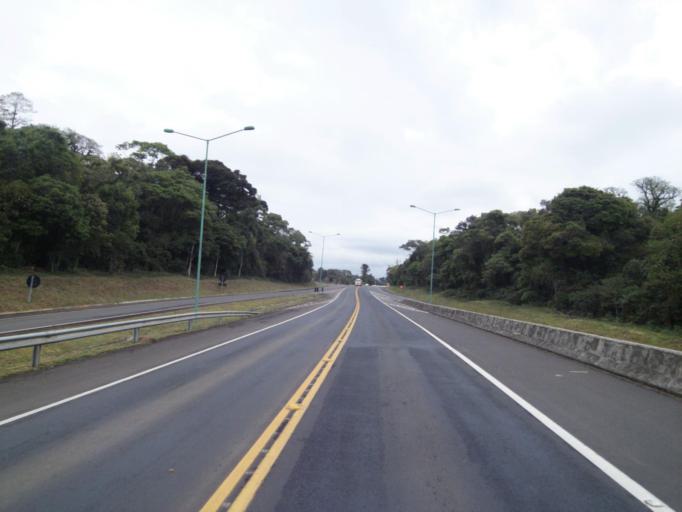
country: BR
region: Parana
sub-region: Irati
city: Irati
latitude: -25.4542
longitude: -50.6207
